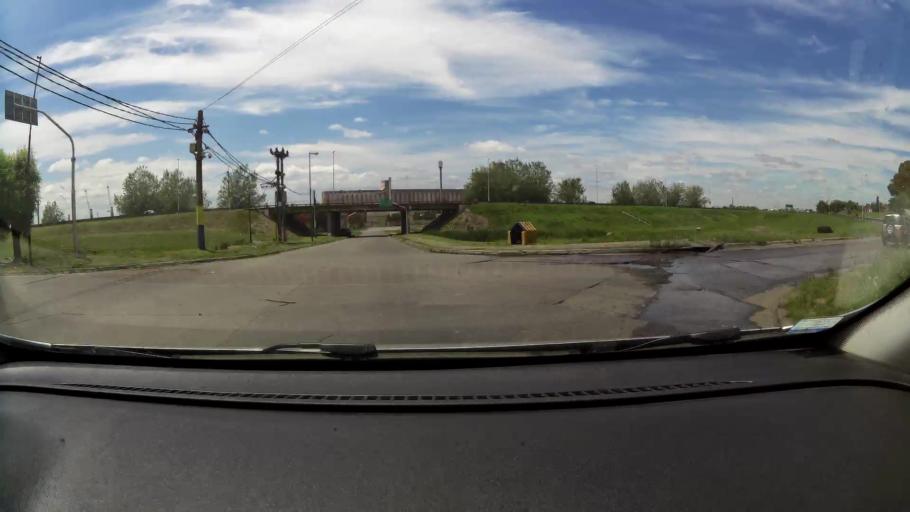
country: AR
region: Santa Fe
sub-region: Departamento de Rosario
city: Rosario
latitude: -32.9803
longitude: -60.6260
